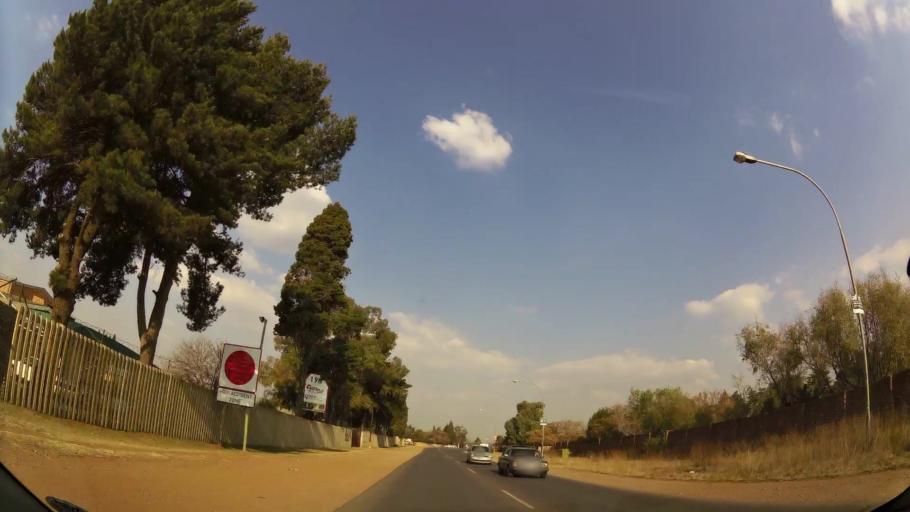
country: ZA
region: Gauteng
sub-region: Ekurhuleni Metropolitan Municipality
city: Benoni
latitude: -26.0934
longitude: 28.2959
